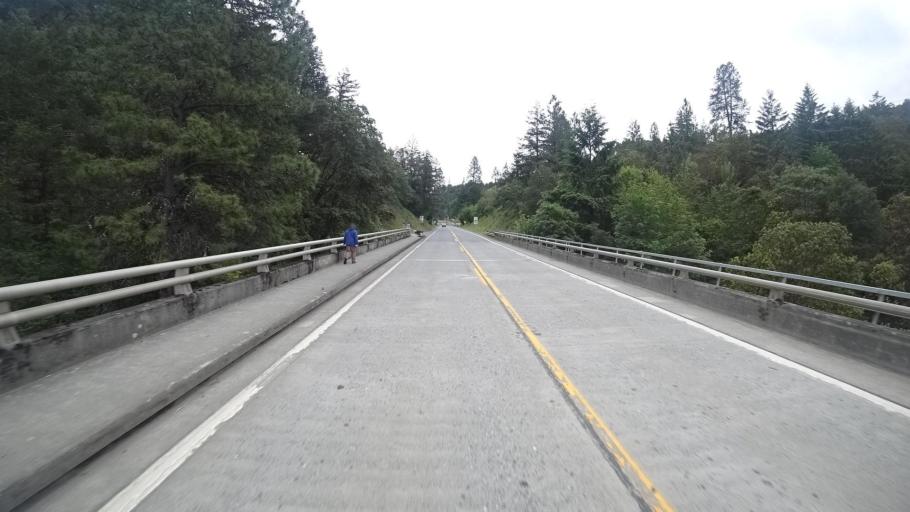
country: US
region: California
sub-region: Humboldt County
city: Willow Creek
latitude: 40.9427
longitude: -123.6329
